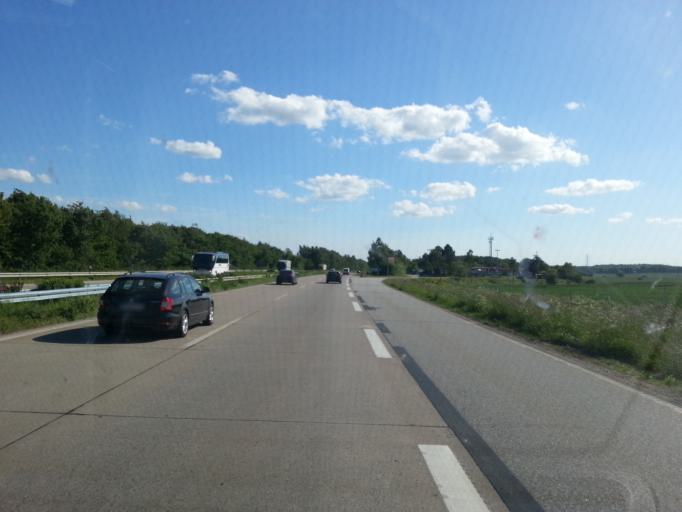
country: DE
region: Schleswig-Holstein
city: Sierksdorf
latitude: 54.0735
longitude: 10.7586
